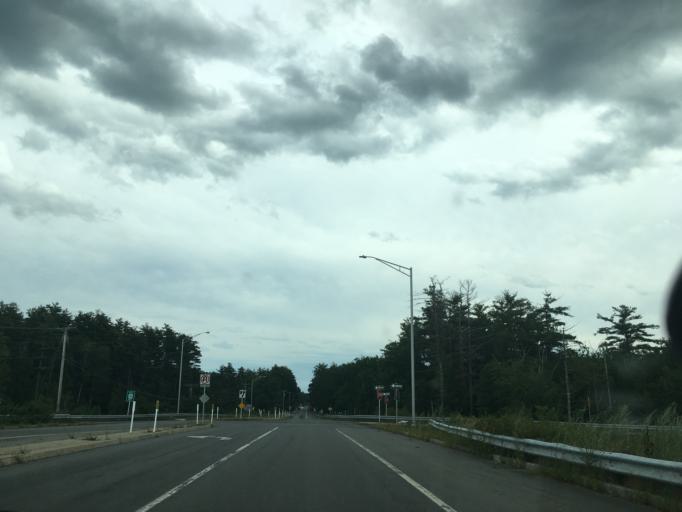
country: US
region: New Hampshire
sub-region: Rockingham County
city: Exeter
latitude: 43.0010
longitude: -70.9758
